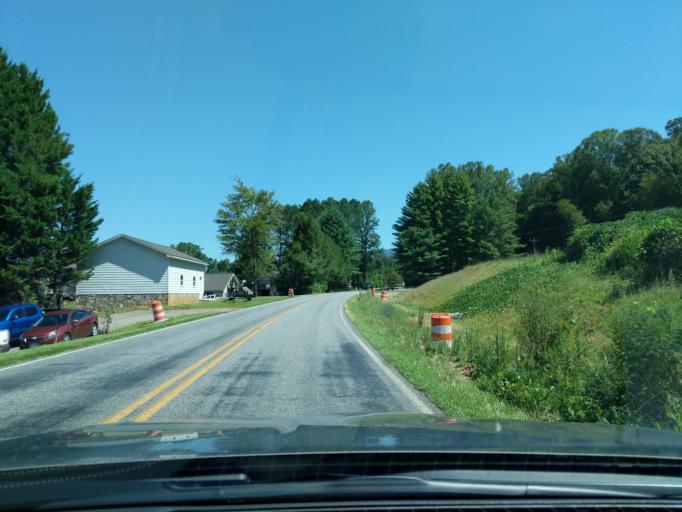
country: US
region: Georgia
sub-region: Towns County
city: Hiawassee
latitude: 35.0056
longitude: -83.7493
